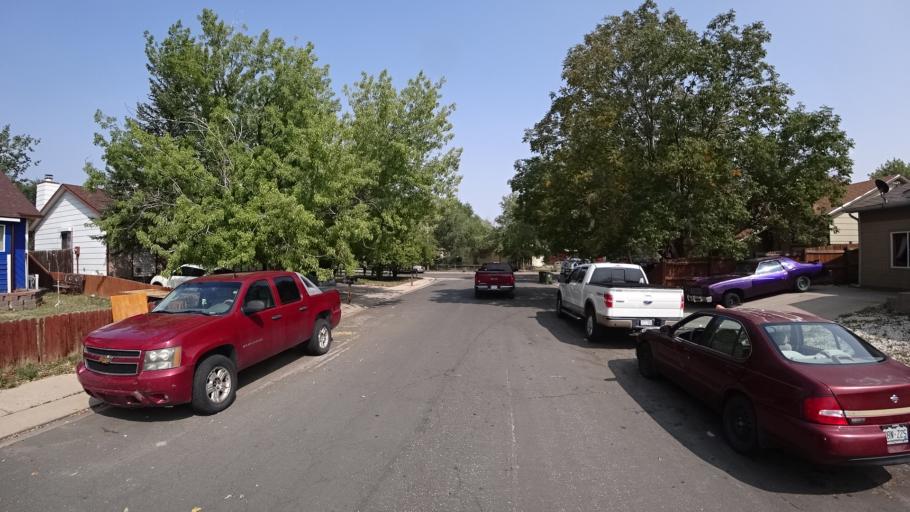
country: US
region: Colorado
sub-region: El Paso County
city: Stratmoor
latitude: 38.8047
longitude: -104.7774
